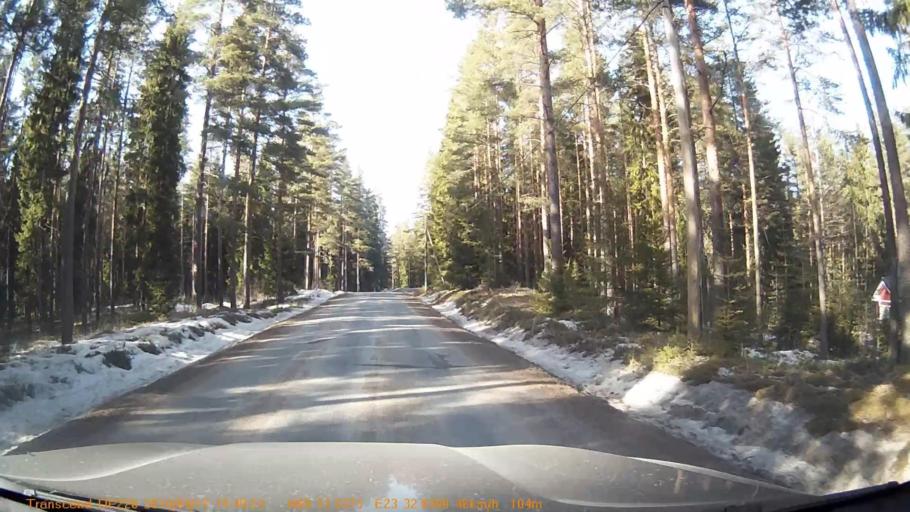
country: FI
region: Haeme
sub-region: Forssa
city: Forssa
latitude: 60.8591
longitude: 23.5488
